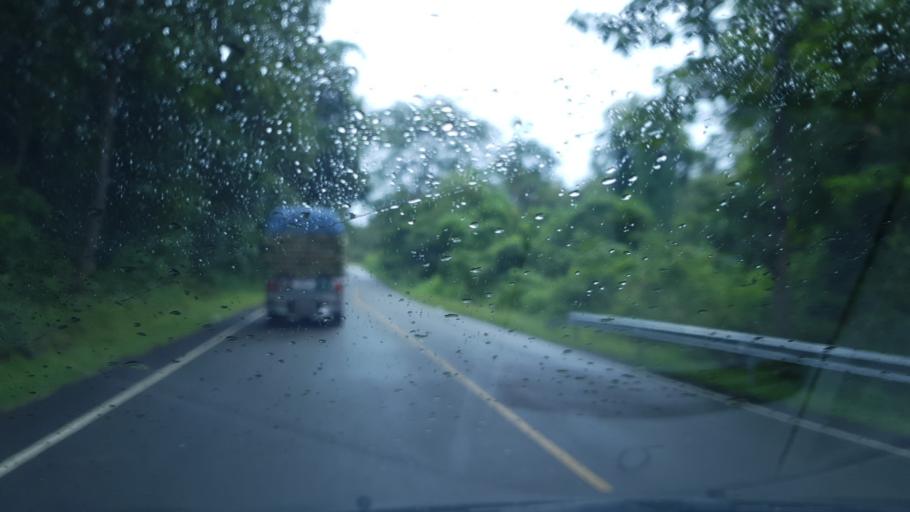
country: TH
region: Mae Hong Son
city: Mae La Noi
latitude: 18.5568
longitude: 97.9315
